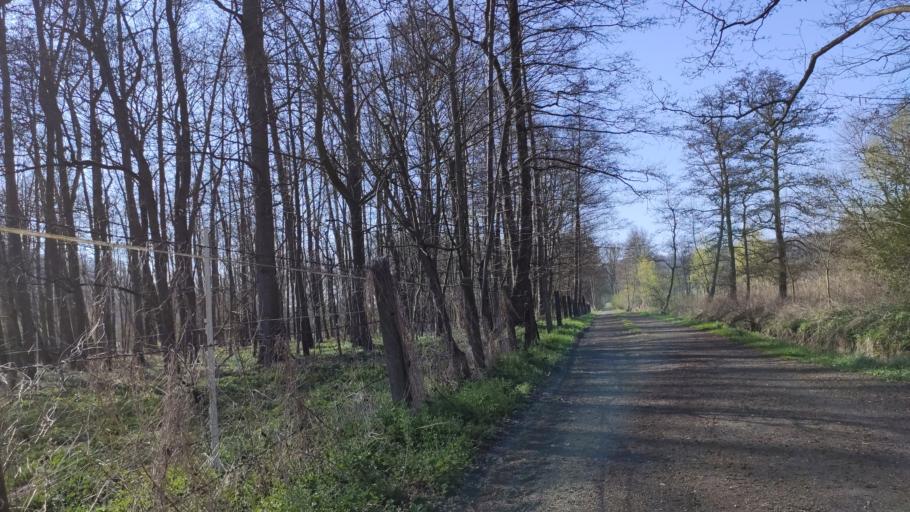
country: DE
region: North Rhine-Westphalia
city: Brakel
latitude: 51.7111
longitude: 9.2821
